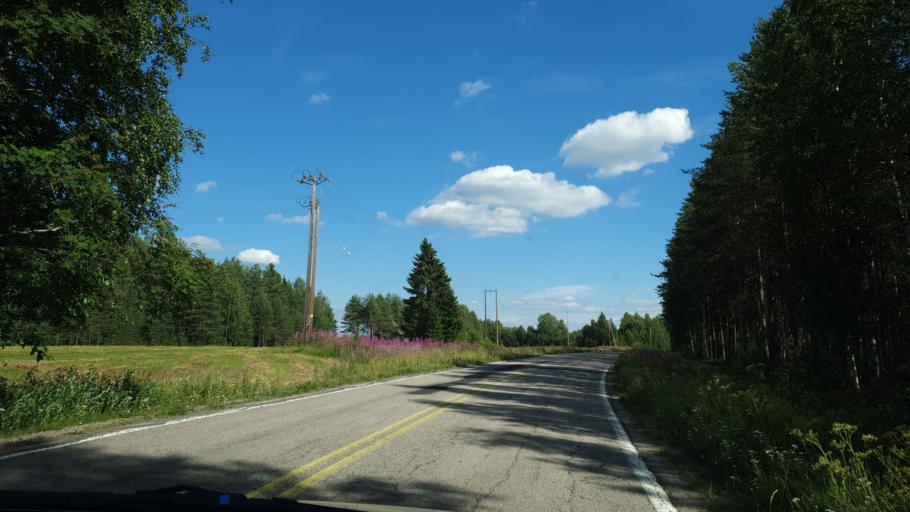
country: FI
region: Kainuu
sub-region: Kehys-Kainuu
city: Kuhmo
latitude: 64.2047
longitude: 29.0482
